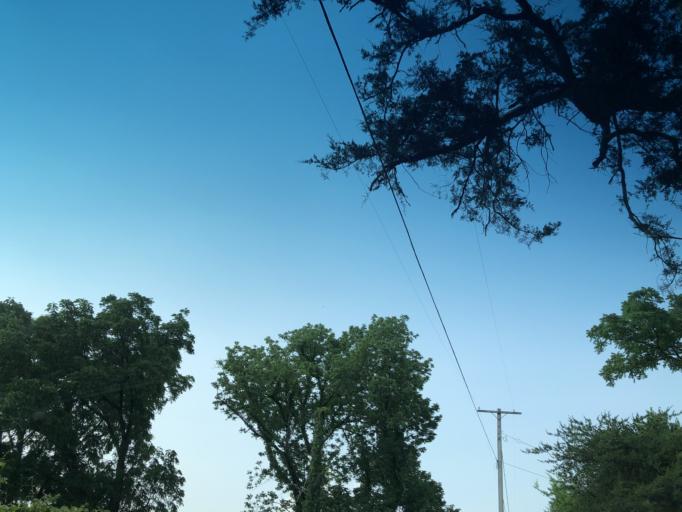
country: US
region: Tennessee
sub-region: Davidson County
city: Goodlettsville
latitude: 36.2756
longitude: -86.7213
